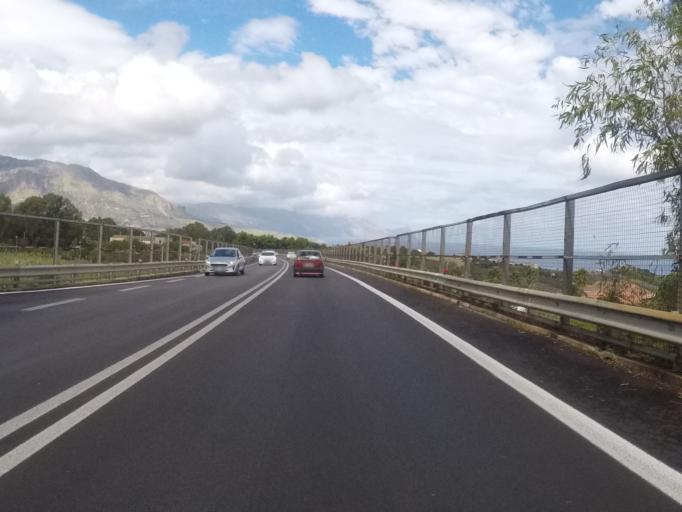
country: IT
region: Sicily
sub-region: Trapani
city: Alcamo
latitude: 38.0104
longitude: 12.9269
